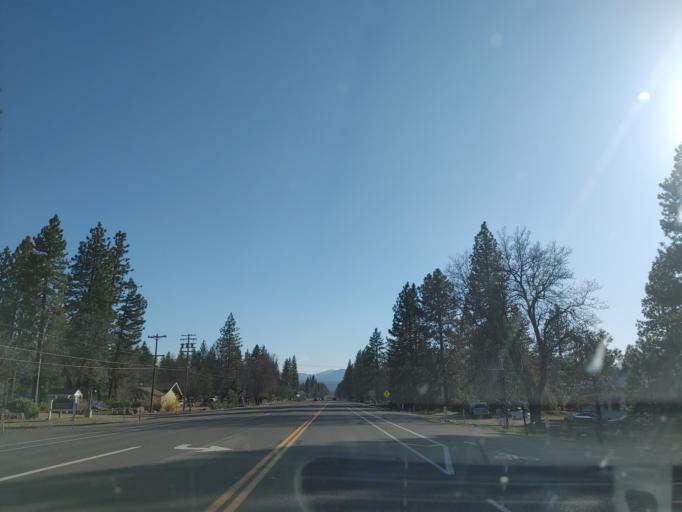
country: US
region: California
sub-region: Shasta County
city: Burney
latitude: 40.9202
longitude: -121.6249
